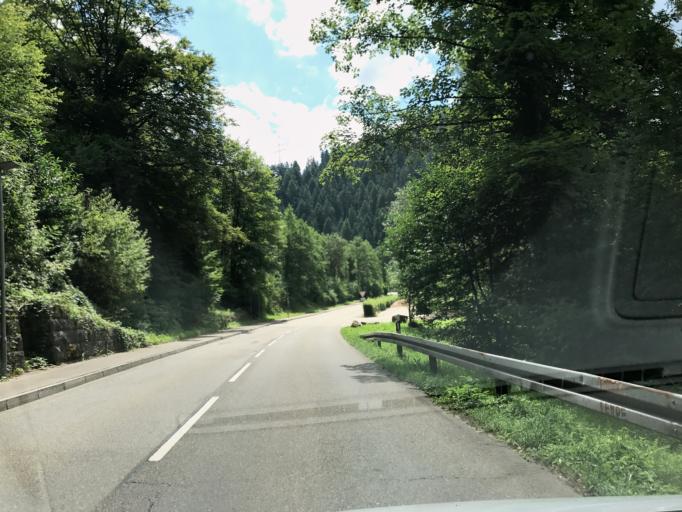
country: DE
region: Baden-Wuerttemberg
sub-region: Freiburg Region
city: Schiltach
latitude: 48.2857
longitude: 8.3465
